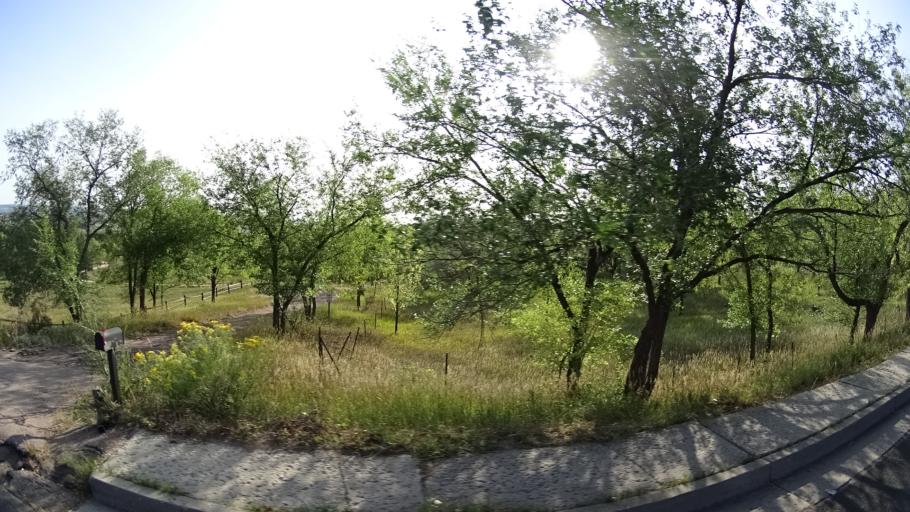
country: US
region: Colorado
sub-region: El Paso County
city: Colorado Springs
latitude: 38.8170
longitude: -104.8594
